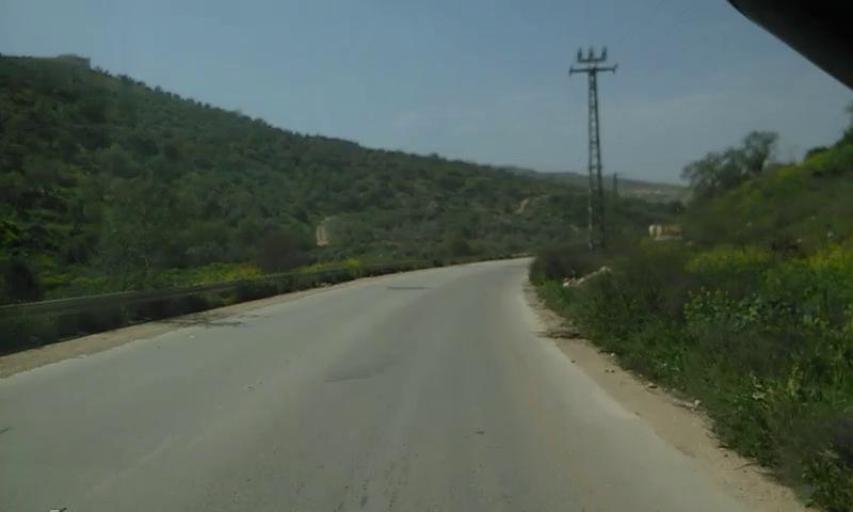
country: PS
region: West Bank
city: Qabatiyah
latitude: 32.4049
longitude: 35.2995
